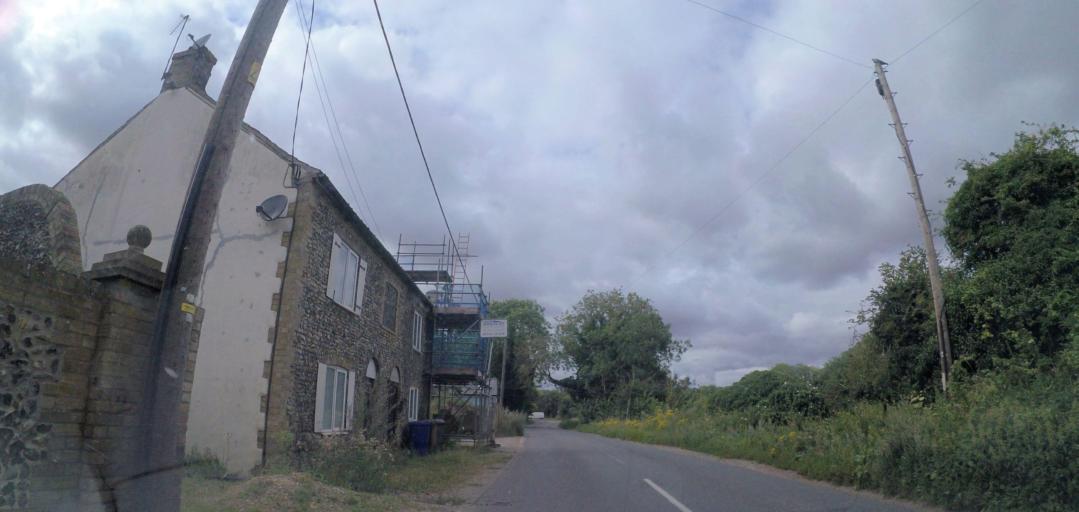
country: GB
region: England
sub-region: Suffolk
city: Lakenheath
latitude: 52.3340
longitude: 0.5339
